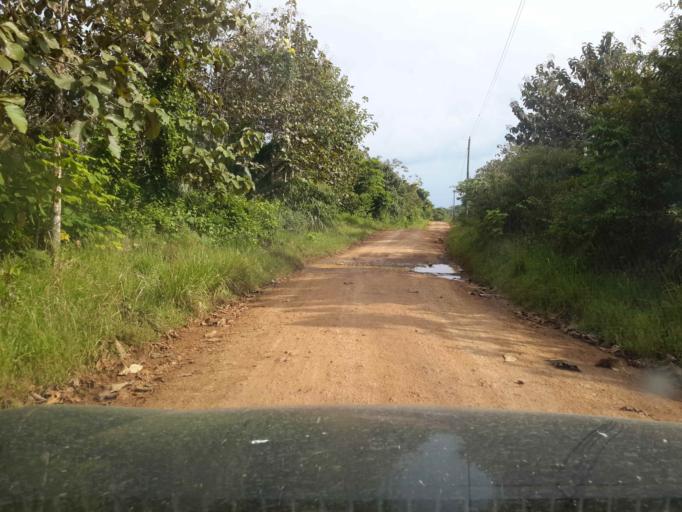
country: CR
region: Alajuela
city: Los Chiles
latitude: 11.0865
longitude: -84.5412
